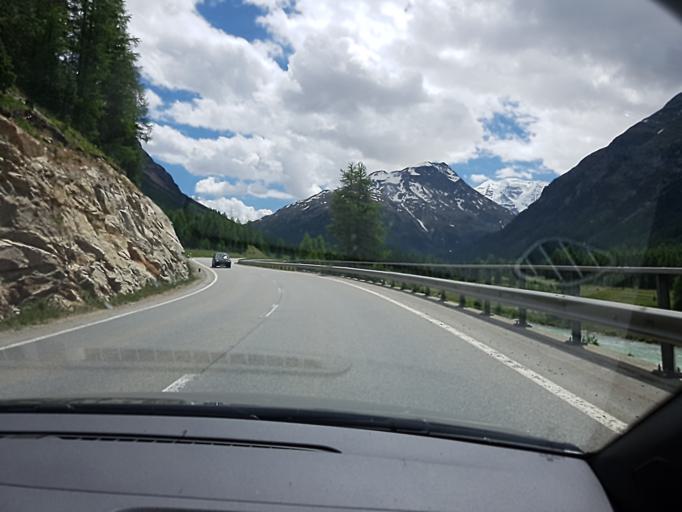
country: CH
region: Grisons
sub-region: Maloja District
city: Pontresina
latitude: 46.4747
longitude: 9.9235
